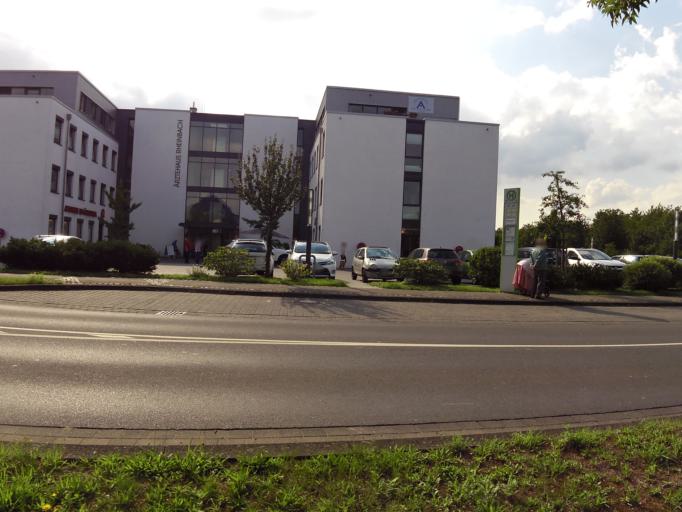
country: DE
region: North Rhine-Westphalia
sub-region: Regierungsbezirk Koln
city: Rheinbach
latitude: 50.6347
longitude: 6.9493
